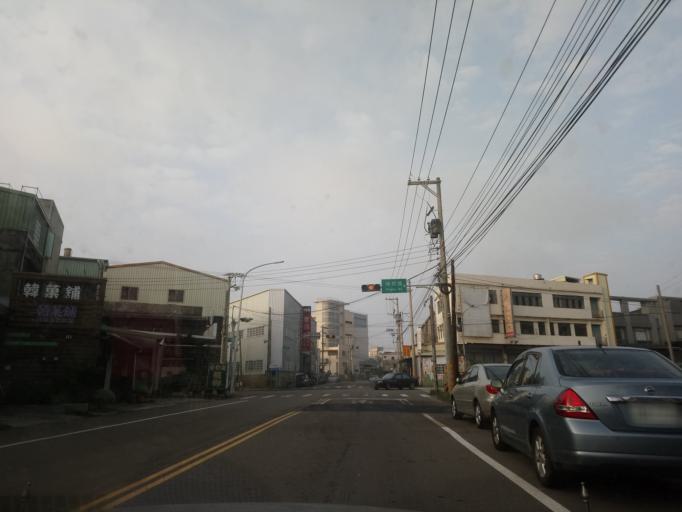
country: TW
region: Taiwan
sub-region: Hsinchu
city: Hsinchu
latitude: 24.7934
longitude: 120.9325
